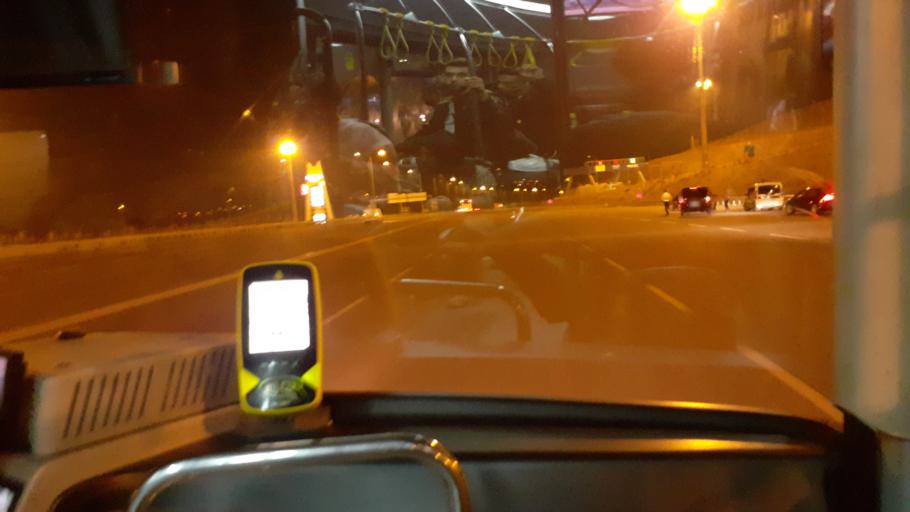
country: TR
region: Istanbul
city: Kemerburgaz
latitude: 41.1964
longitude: 28.8238
